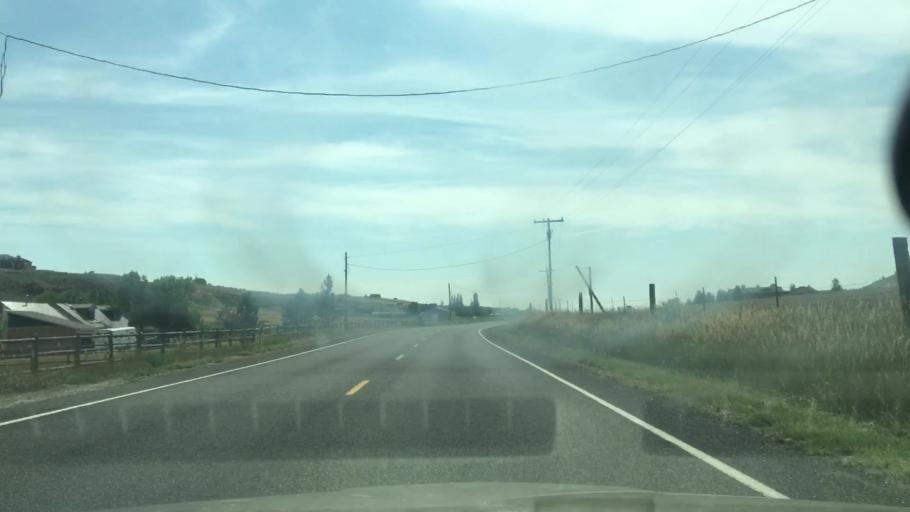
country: US
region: Colorado
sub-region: Larimer County
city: Campion
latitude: 40.3581
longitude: -105.1856
